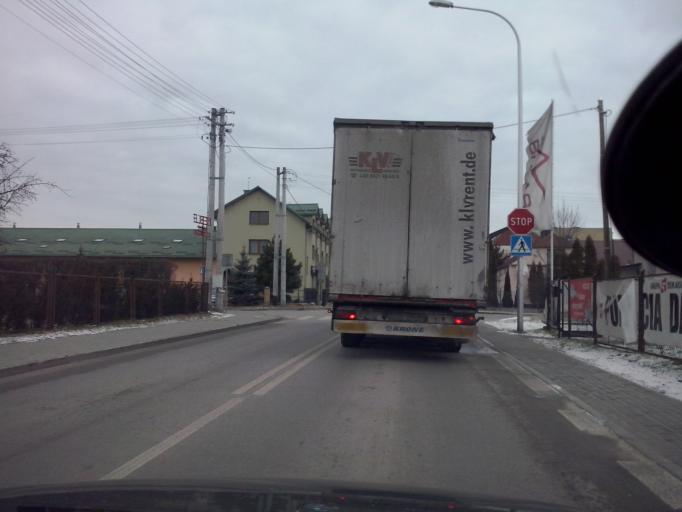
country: PL
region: Lublin Voivodeship
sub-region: Powiat bilgorajski
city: Bilgoraj
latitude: 50.5290
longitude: 22.7230
